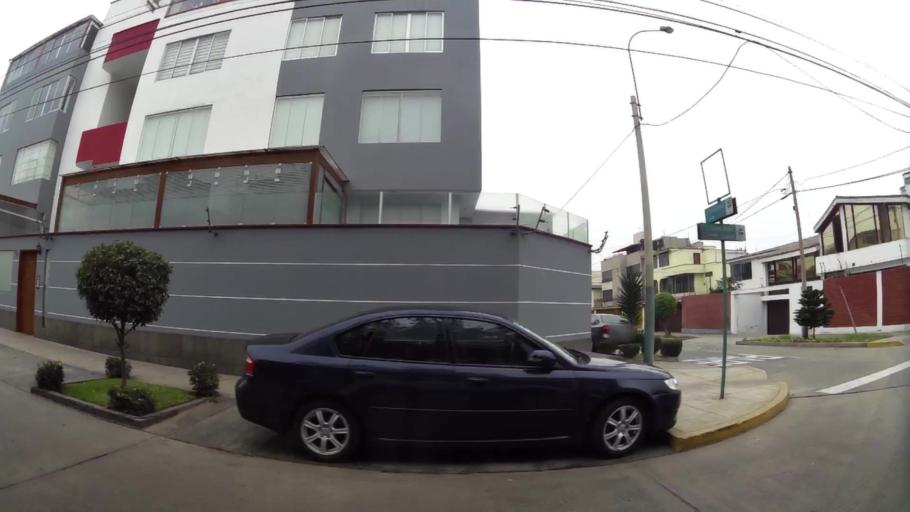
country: PE
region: Lima
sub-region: Lima
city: San Luis
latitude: -12.1020
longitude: -77.0051
